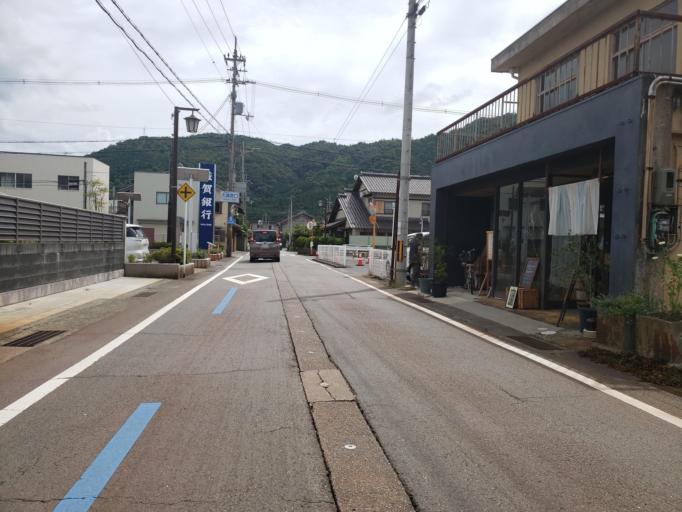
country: JP
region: Shiga Prefecture
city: Kitahama
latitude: 35.2953
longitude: 136.0120
